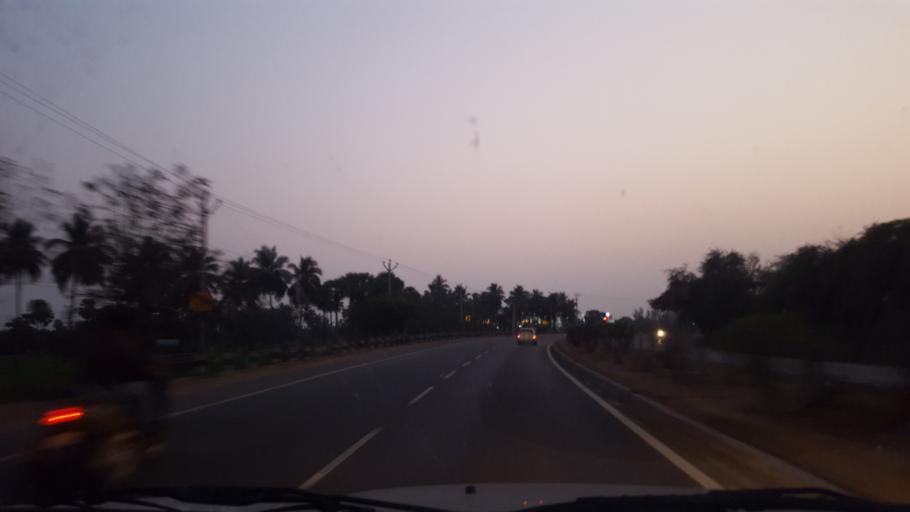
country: IN
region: Andhra Pradesh
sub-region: East Godavari
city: Peddapuram
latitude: 17.1496
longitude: 81.9851
